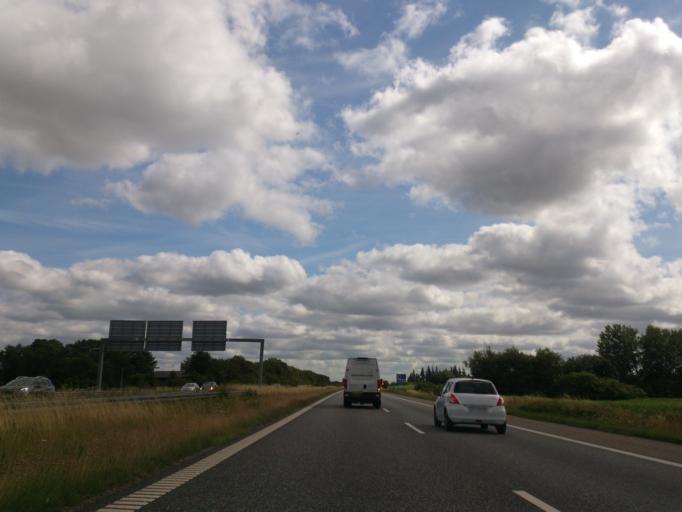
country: DK
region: South Denmark
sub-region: Aabenraa Kommune
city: Krusa
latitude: 54.9315
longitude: 9.3836
